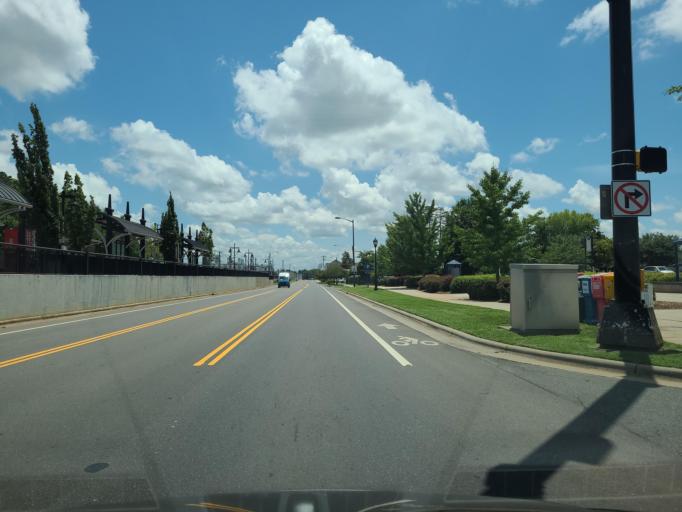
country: US
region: North Carolina
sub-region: Mecklenburg County
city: Charlotte
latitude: 35.1762
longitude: -80.8794
